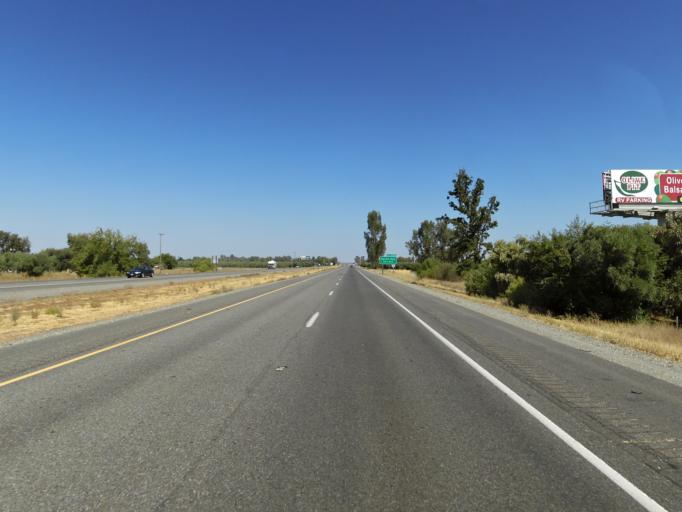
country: US
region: California
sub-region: Tehama County
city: Corning
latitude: 39.8872
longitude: -122.2000
